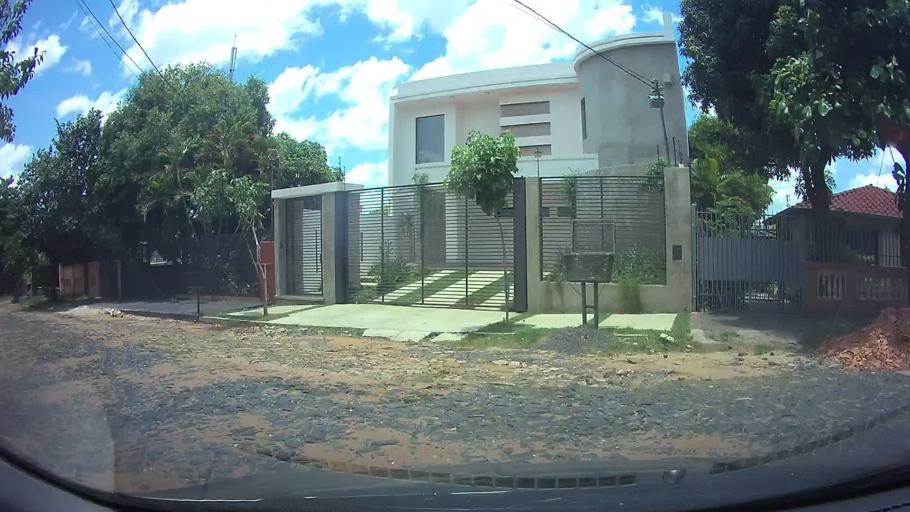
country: PY
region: Asuncion
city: Asuncion
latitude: -25.2730
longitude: -57.5904
